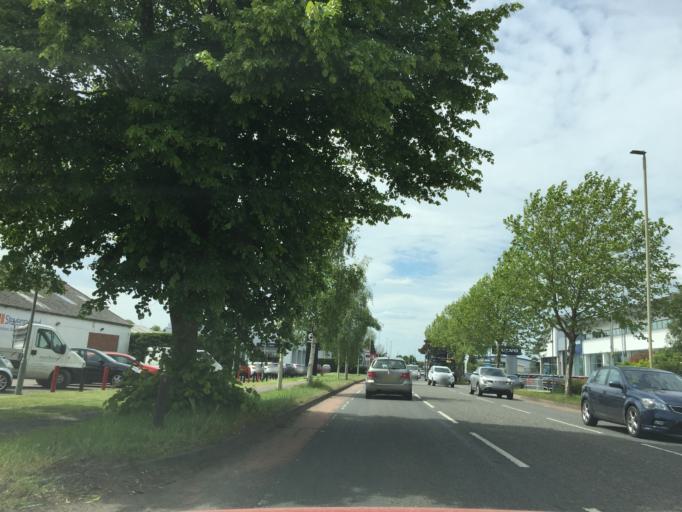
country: GB
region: England
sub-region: Gloucestershire
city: Gloucester
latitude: 51.8364
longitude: -2.2650
